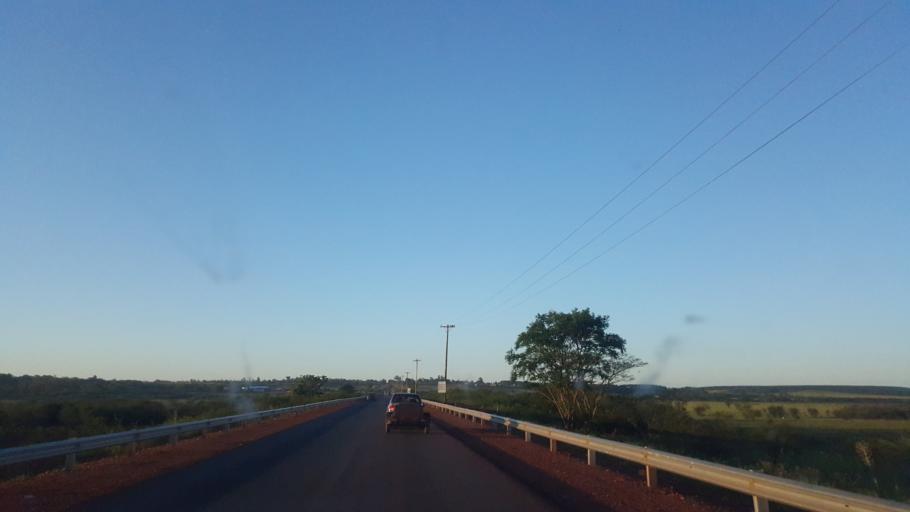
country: AR
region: Corrientes
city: Santo Tome
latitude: -28.5412
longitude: -56.0499
